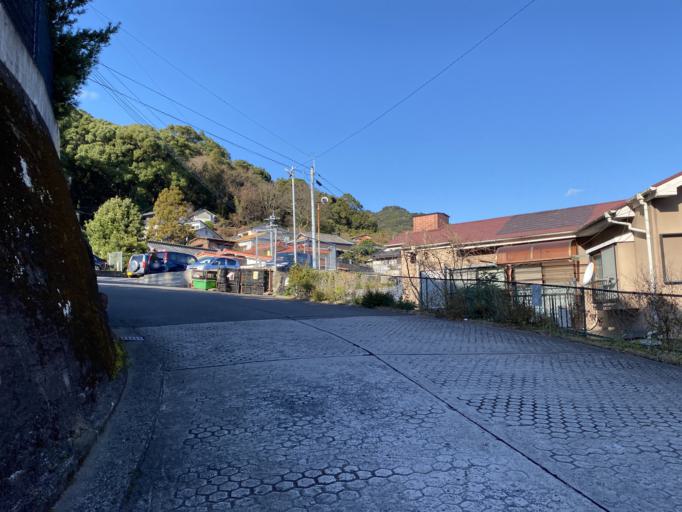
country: JP
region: Nagasaki
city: Nagasaki-shi
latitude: 32.7588
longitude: 129.8600
